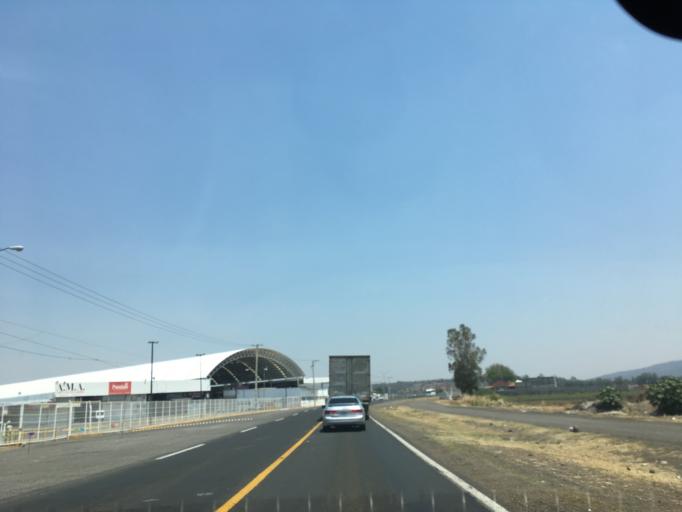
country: MX
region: Michoacan
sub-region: Cuitzeo
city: Cuamio
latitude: 20.0683
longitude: -101.1547
